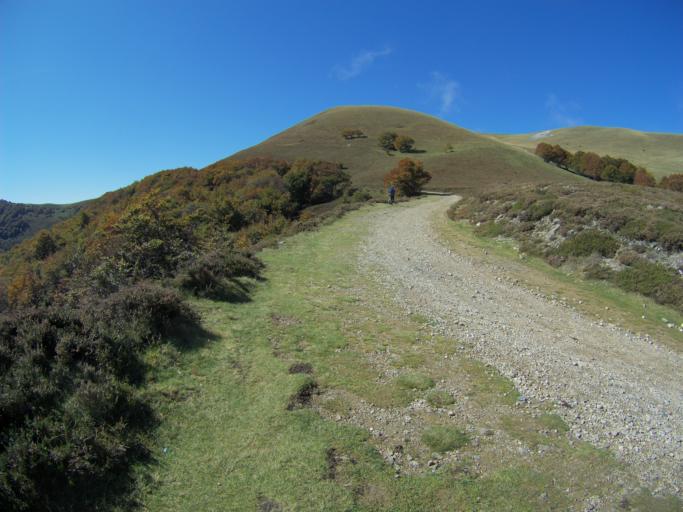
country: ES
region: Navarre
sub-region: Provincia de Navarra
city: Orbara
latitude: 43.0348
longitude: -1.2909
